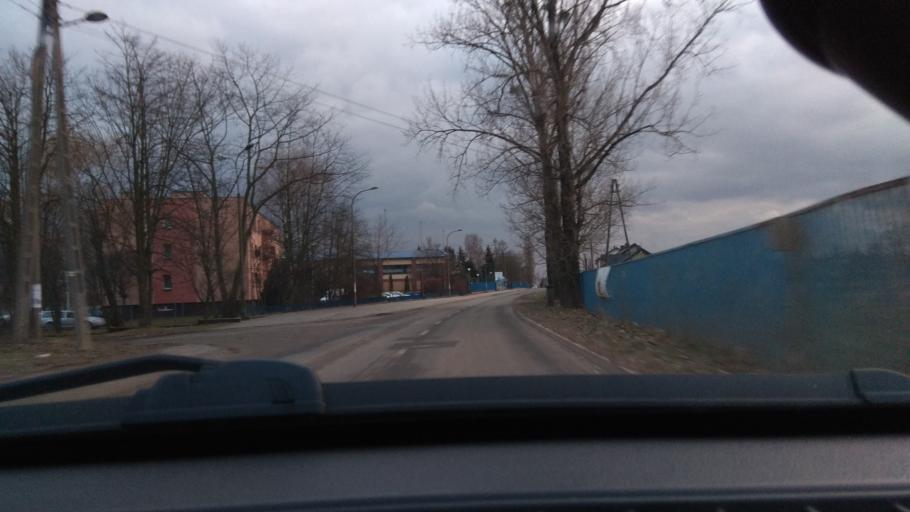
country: PL
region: Greater Poland Voivodeship
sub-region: Powiat kepinski
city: Kepno
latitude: 51.2994
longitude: 18.0059
